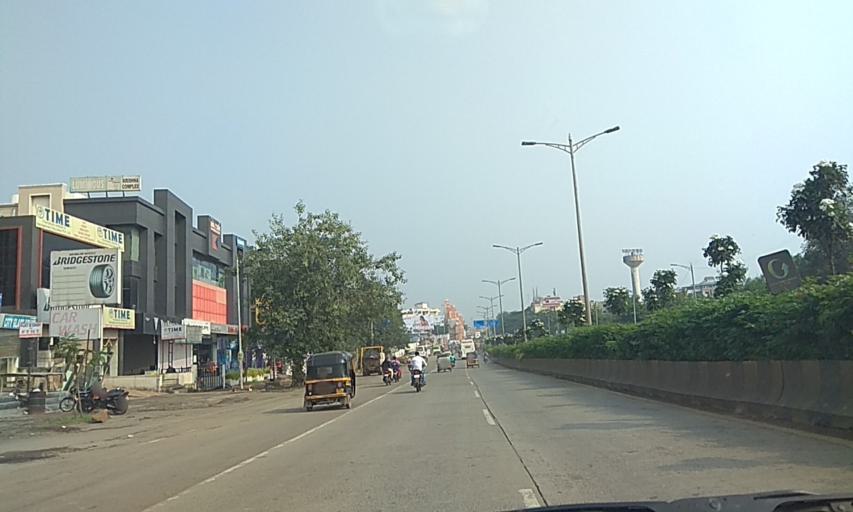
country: IN
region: Maharashtra
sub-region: Pune Division
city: Lohogaon
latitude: 18.5558
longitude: 73.9377
